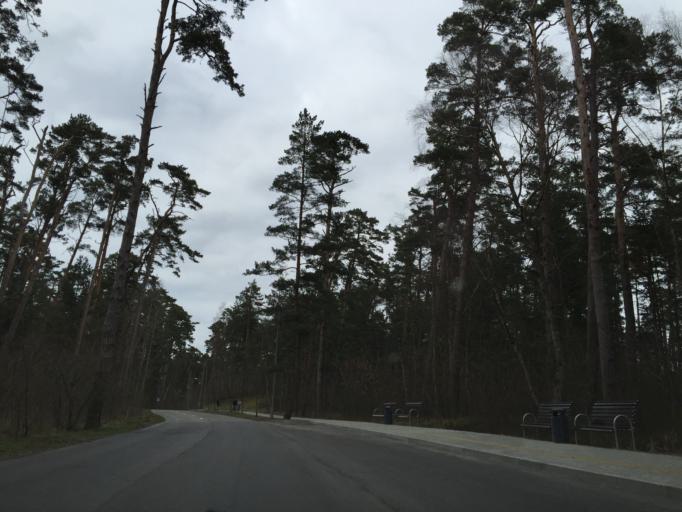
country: LT
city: Nida
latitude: 55.3138
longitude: 21.0110
